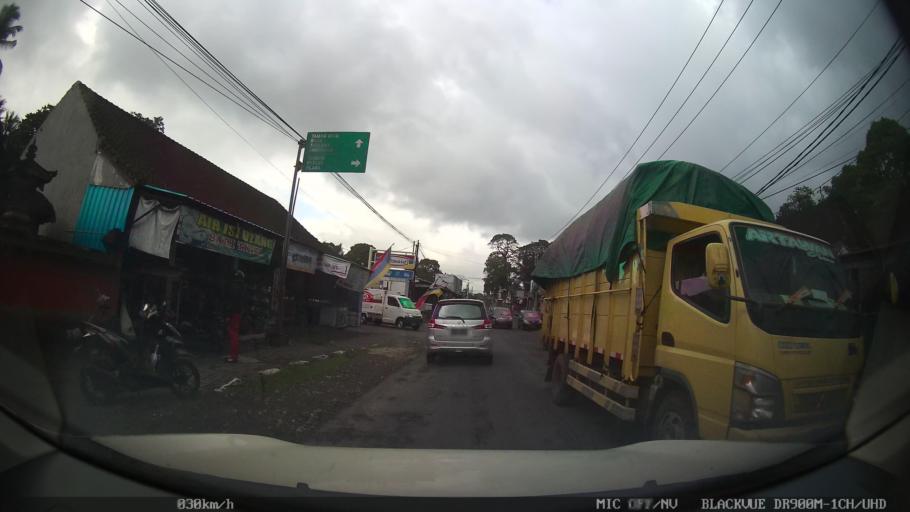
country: ID
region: Bali
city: Banjar Keraman
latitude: -8.5257
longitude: 115.2108
